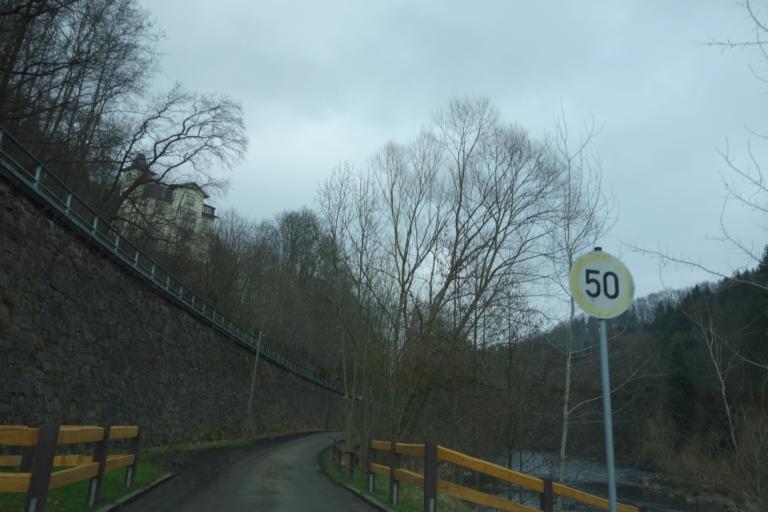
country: DE
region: Saxony
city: Grunhainichen
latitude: 50.7692
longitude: 13.1625
